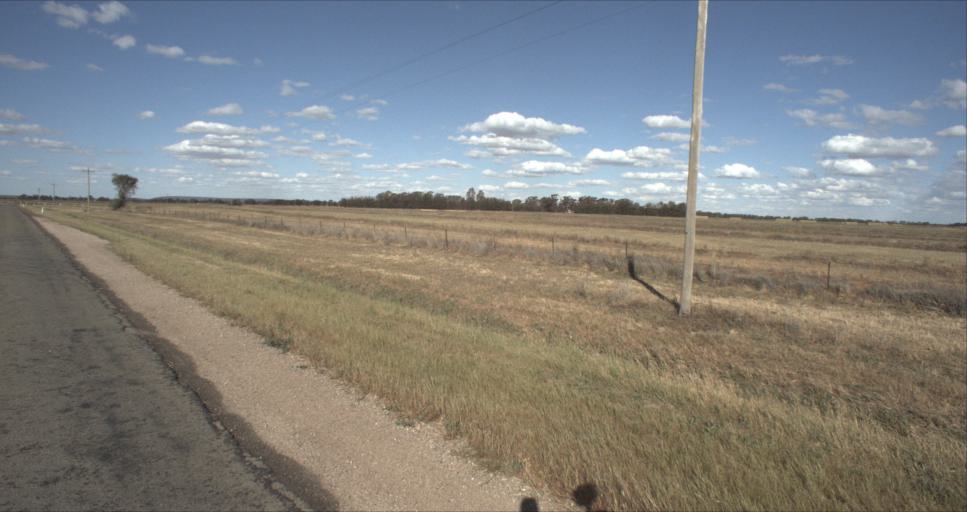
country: AU
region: New South Wales
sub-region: Leeton
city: Leeton
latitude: -34.4570
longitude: 146.2720
